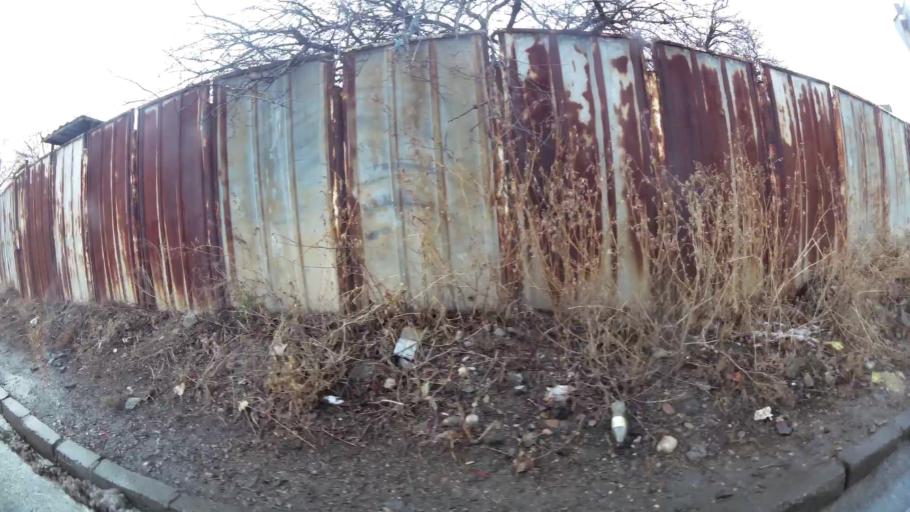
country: BG
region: Sofia-Capital
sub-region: Stolichna Obshtina
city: Sofia
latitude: 42.6997
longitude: 23.3871
